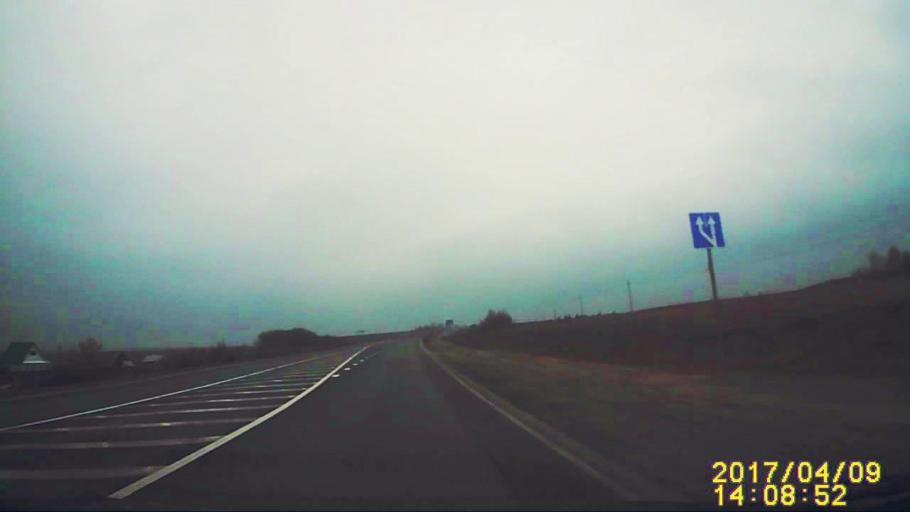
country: RU
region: Ulyanovsk
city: Silikatnyy
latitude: 54.0238
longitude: 48.2144
